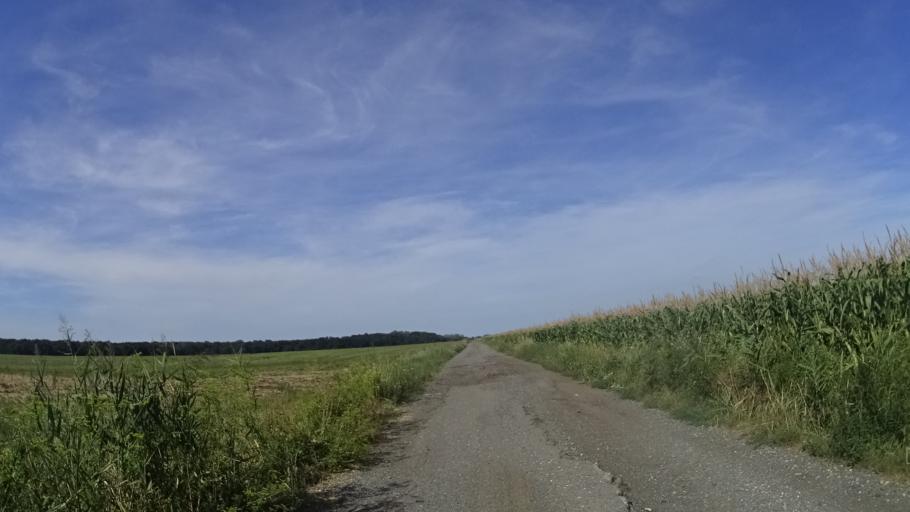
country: AT
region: Lower Austria
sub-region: Politischer Bezirk Ganserndorf
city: Durnkrut
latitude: 48.4491
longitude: 16.8837
